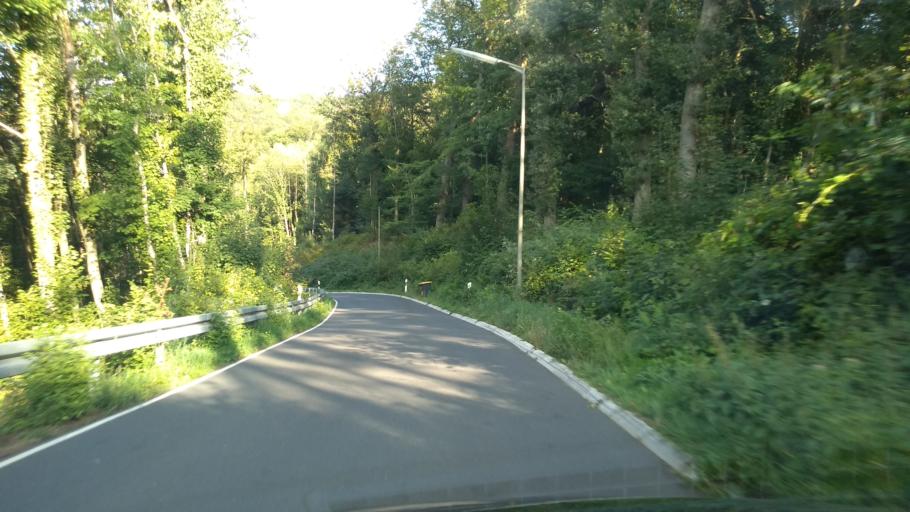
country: DE
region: North Rhine-Westphalia
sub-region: Regierungsbezirk Koln
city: Engelskirchen
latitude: 50.9834
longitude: 7.4509
